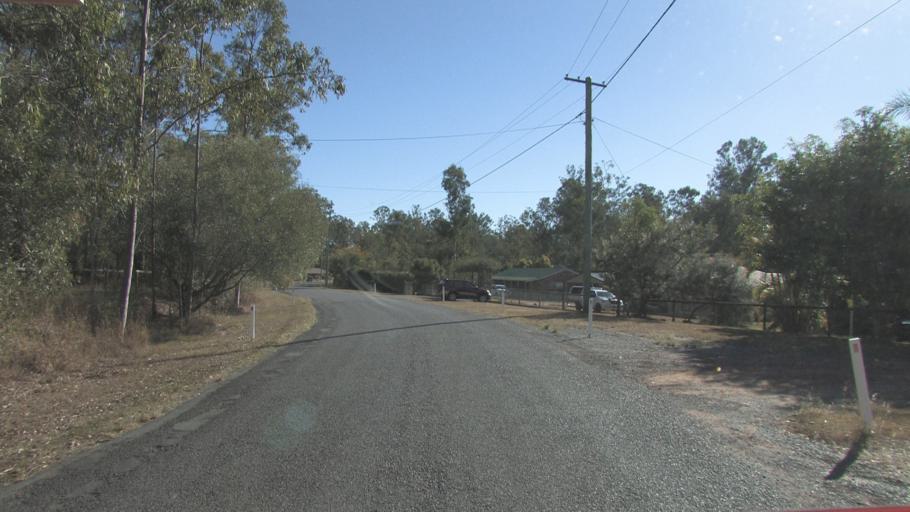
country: AU
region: Queensland
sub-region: Logan
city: North Maclean
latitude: -27.8084
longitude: 152.9886
